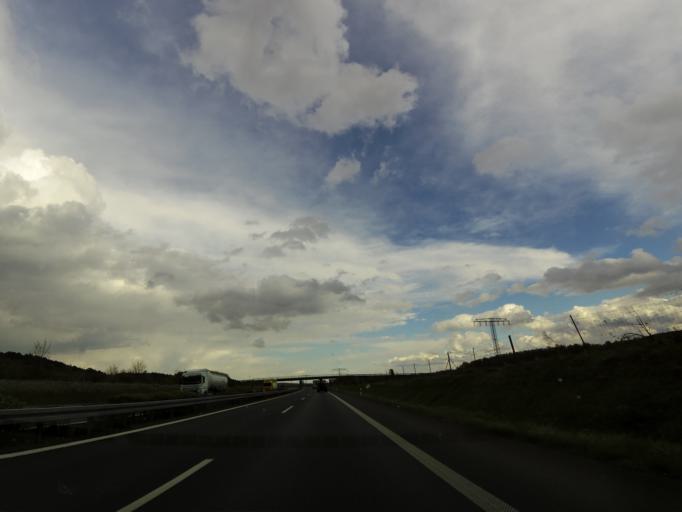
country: DE
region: Saxony-Anhalt
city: Blankenburg
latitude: 51.8070
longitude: 10.9560
